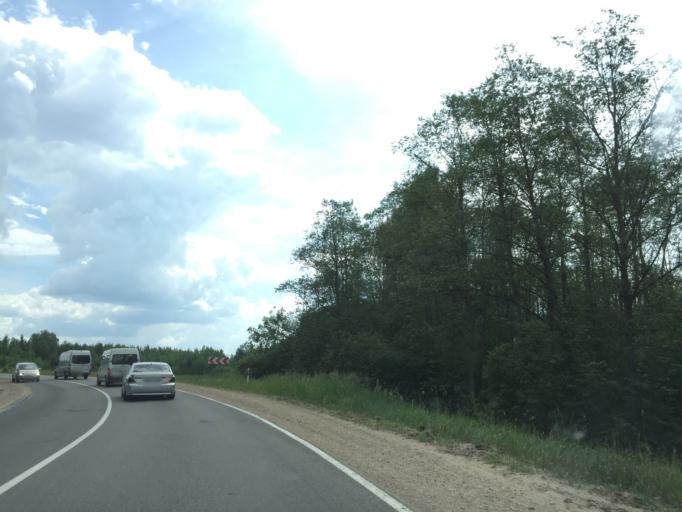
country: LV
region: Salas
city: Sala
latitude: 56.5470
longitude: 25.8013
